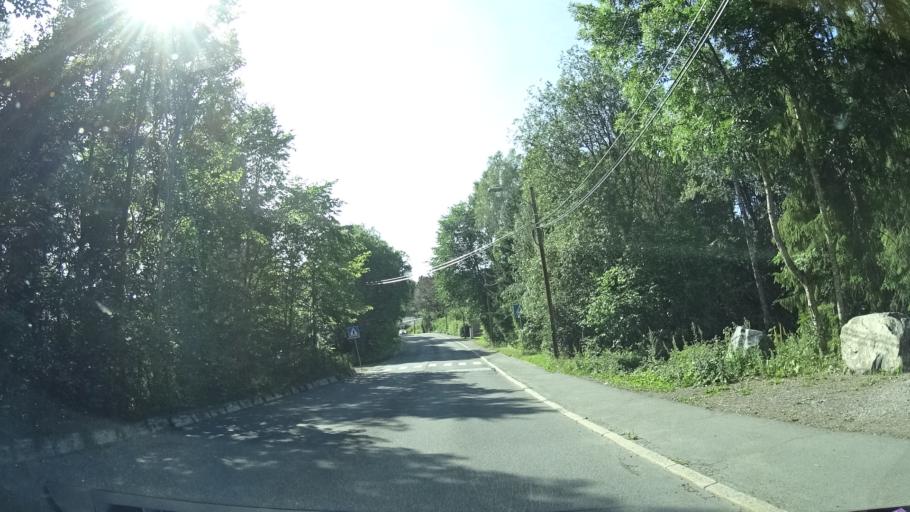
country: NO
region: Oslo
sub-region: Oslo
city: Sjolyststranda
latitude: 59.9595
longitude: 10.6834
